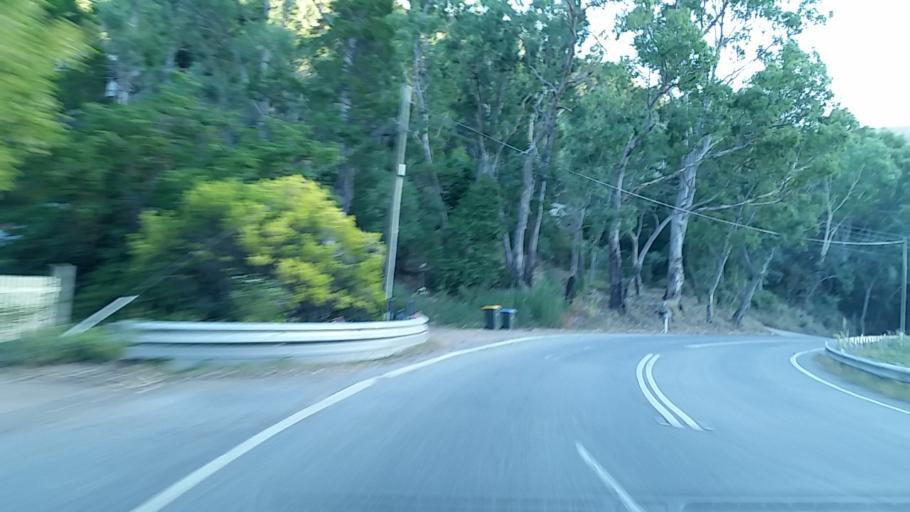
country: AU
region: South Australia
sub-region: Campbelltown
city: Athelstone
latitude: -34.8684
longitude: 138.7563
